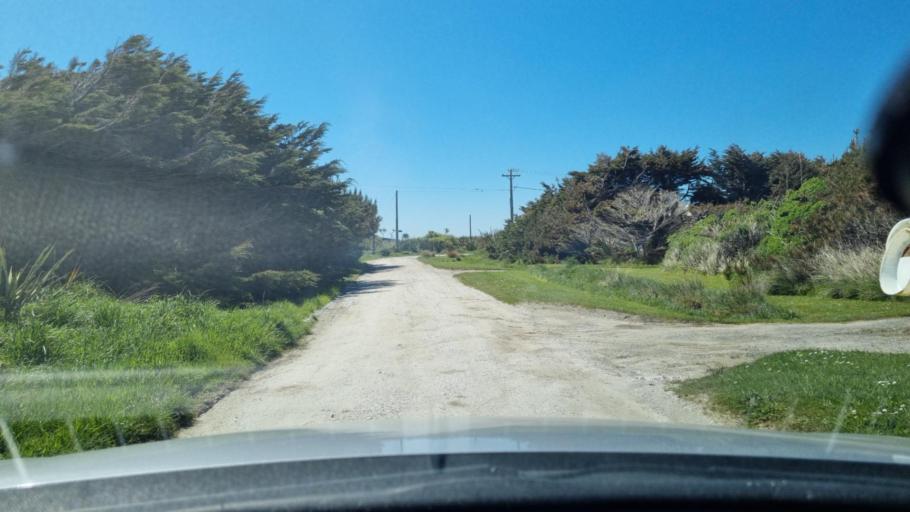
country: NZ
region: Southland
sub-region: Invercargill City
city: Invercargill
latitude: -46.4297
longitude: 168.2304
